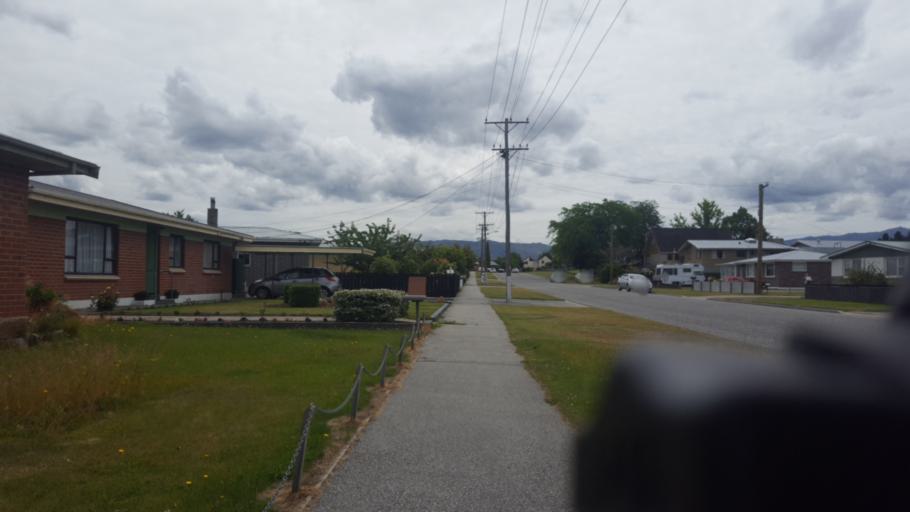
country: NZ
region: Otago
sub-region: Queenstown-Lakes District
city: Wanaka
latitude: -45.2483
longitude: 169.3800
